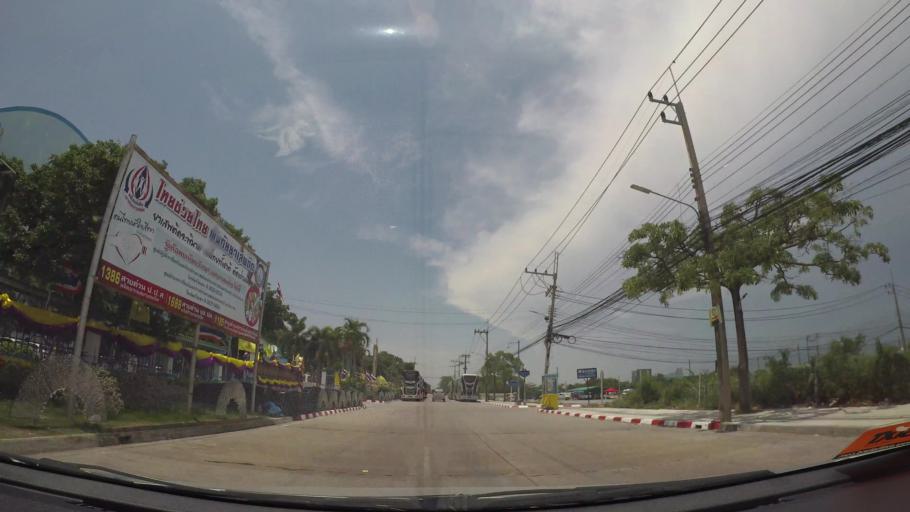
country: TH
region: Chon Buri
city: Chon Buri
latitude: 13.3421
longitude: 100.9461
